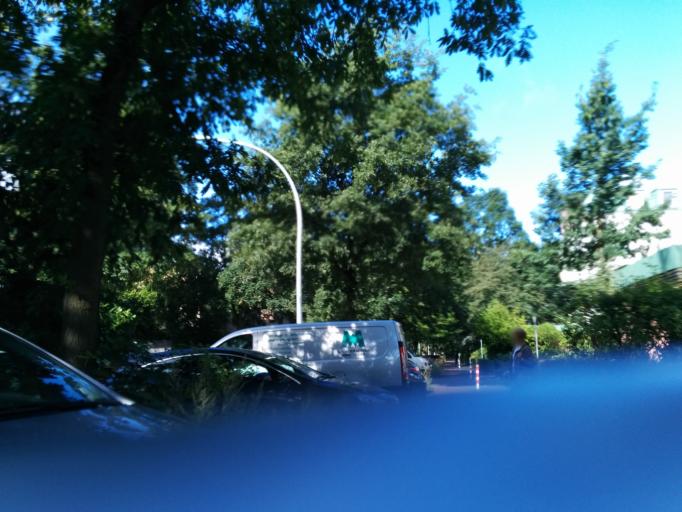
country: DE
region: Hamburg
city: Altona
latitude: 53.5495
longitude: 9.9067
